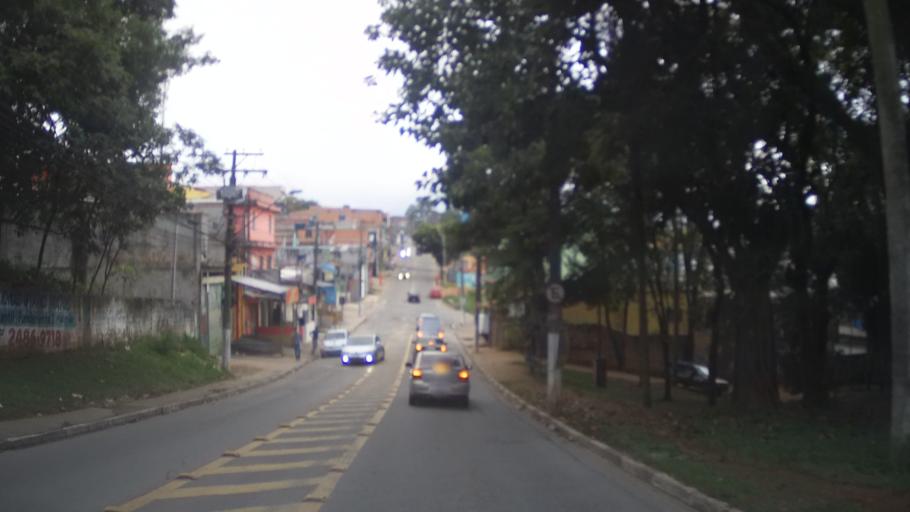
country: BR
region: Sao Paulo
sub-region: Itaquaquecetuba
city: Itaquaquecetuba
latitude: -23.4510
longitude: -46.4238
